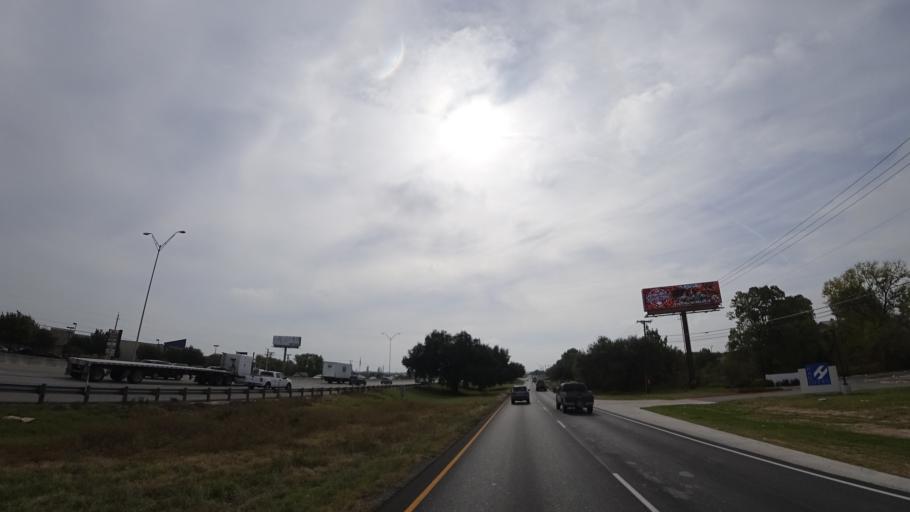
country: US
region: Texas
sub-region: Travis County
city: Windemere
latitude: 30.4766
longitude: -97.6732
